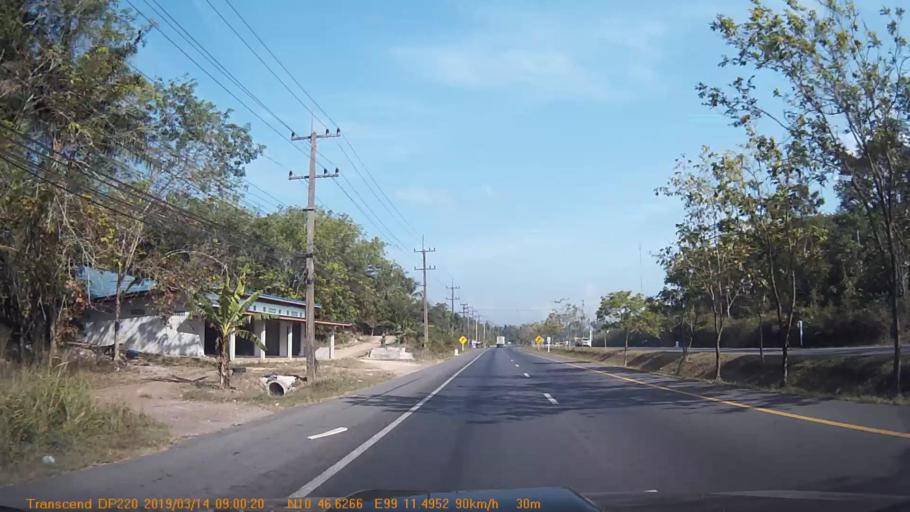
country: TH
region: Chumphon
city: Tha Sae
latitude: 10.7775
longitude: 99.1914
